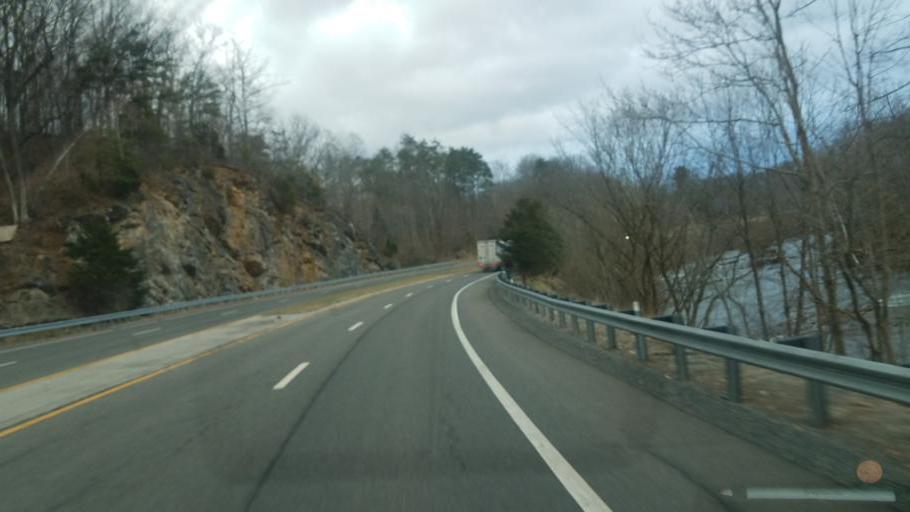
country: US
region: Virginia
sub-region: Giles County
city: Pearisburg
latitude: 37.2520
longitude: -80.7070
